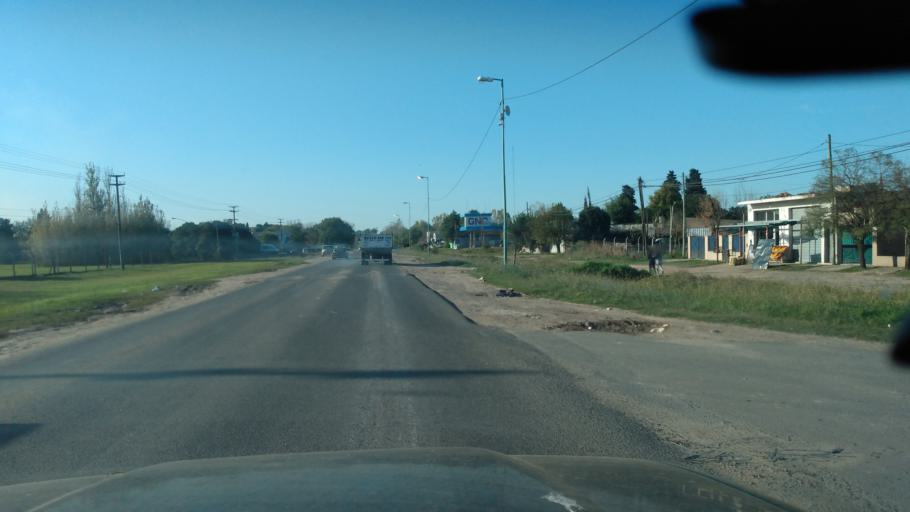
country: AR
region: Buenos Aires
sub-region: Partido de Lujan
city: Lujan
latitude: -34.5421
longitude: -59.1212
